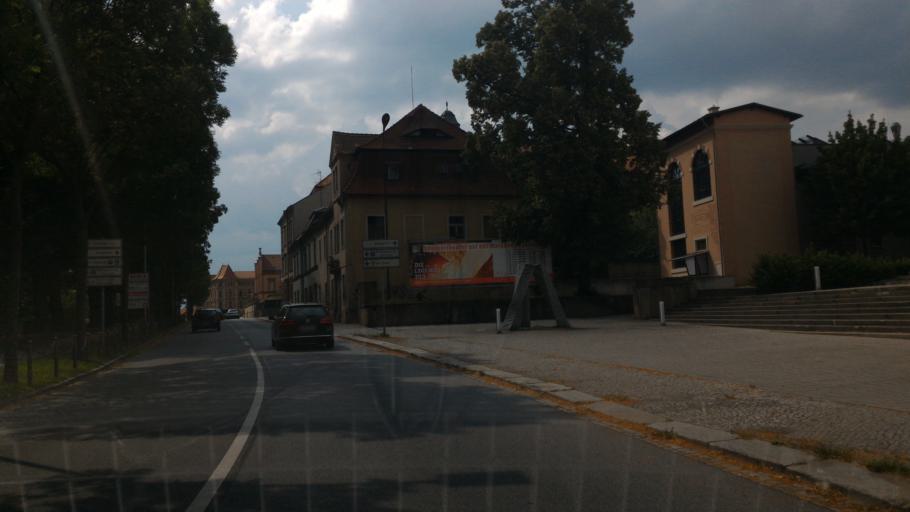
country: DE
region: Saxony
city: Zittau
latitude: 50.8989
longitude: 14.8092
